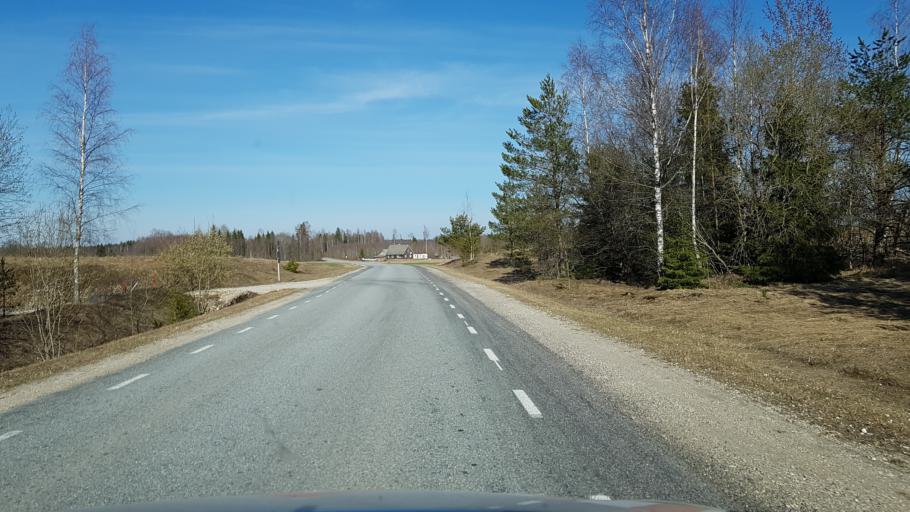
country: EE
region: Laeaene-Virumaa
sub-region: Rakke vald
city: Rakke
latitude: 59.0068
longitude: 26.3273
